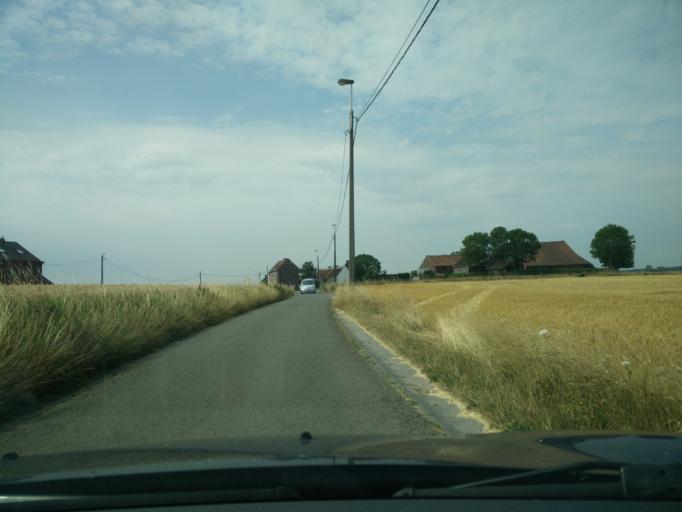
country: BE
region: Flanders
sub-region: Provincie Vlaams-Brabant
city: Halle
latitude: 50.7028
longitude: 4.2327
